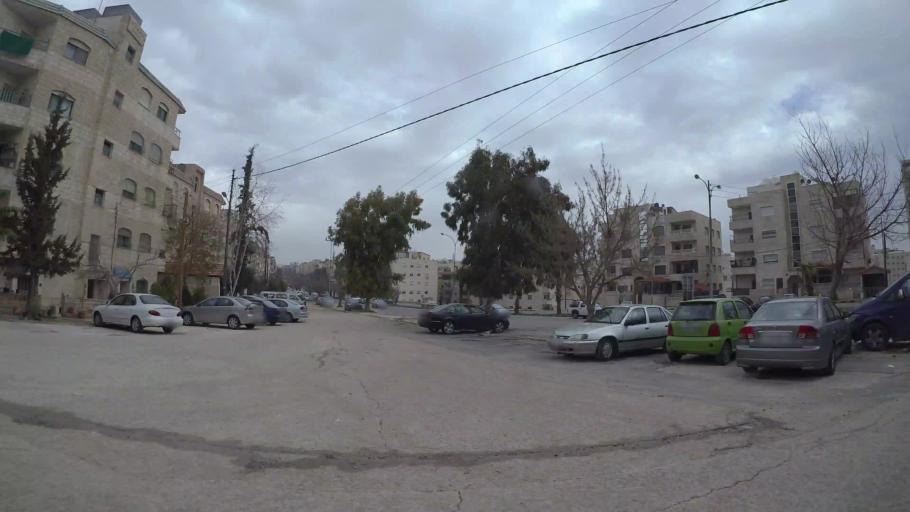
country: JO
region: Amman
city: Amman
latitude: 31.9771
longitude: 35.9332
